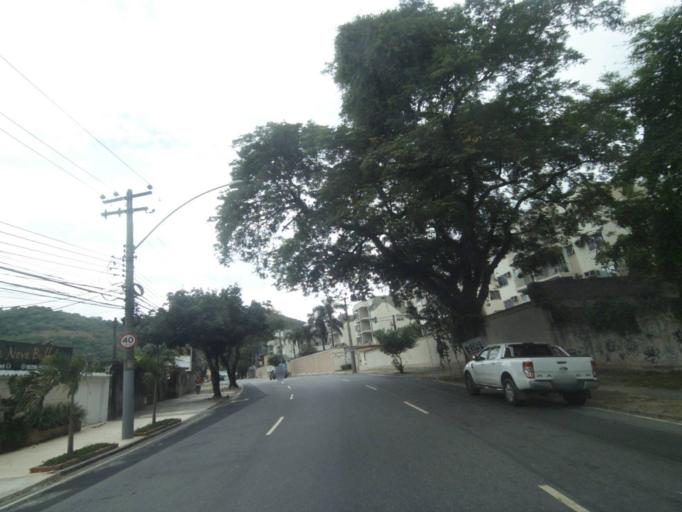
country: BR
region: Rio de Janeiro
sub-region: Nilopolis
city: Nilopolis
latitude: -22.8886
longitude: -43.3945
